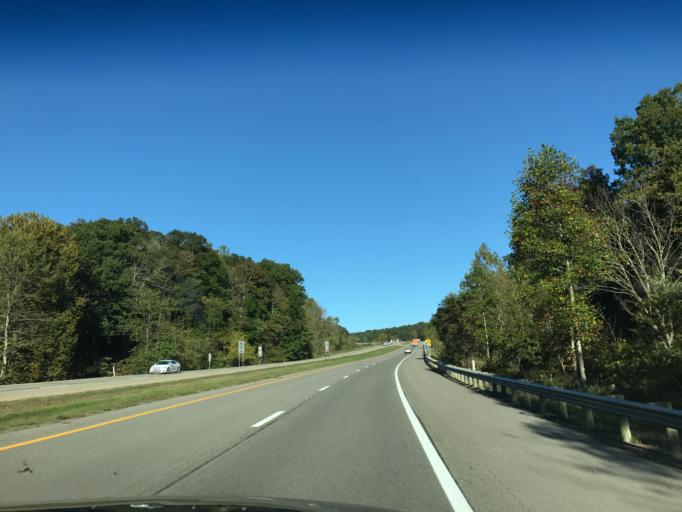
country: US
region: Ohio
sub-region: Washington County
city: Newport
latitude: 39.2486
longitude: -81.2415
